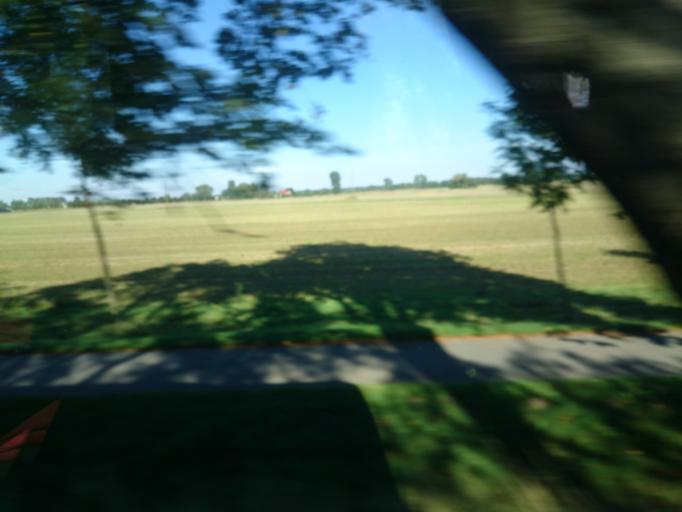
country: DE
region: Mecklenburg-Vorpommern
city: Ducherow
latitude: 53.7503
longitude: 13.7802
